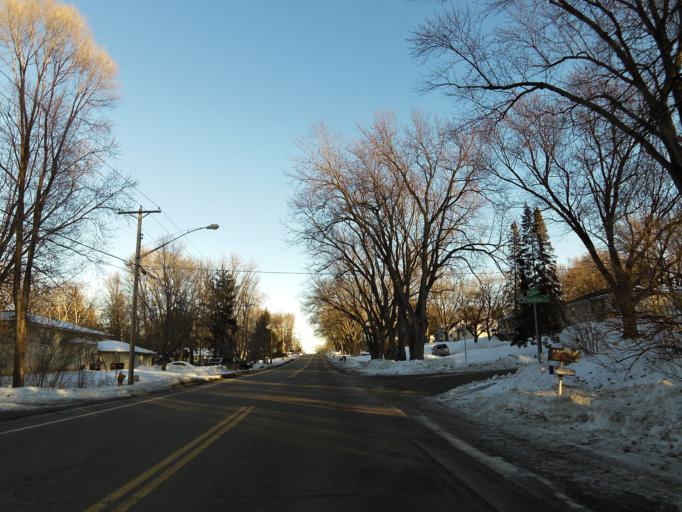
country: US
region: Minnesota
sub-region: Ramsey County
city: North Saint Paul
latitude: 45.0209
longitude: -93.0294
